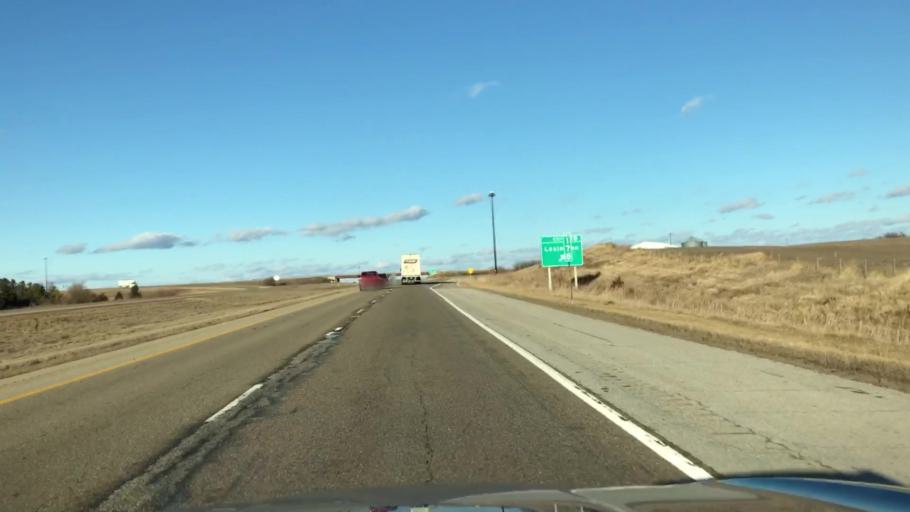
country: US
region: Illinois
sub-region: McLean County
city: Lexington
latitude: 40.6399
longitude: -88.8117
